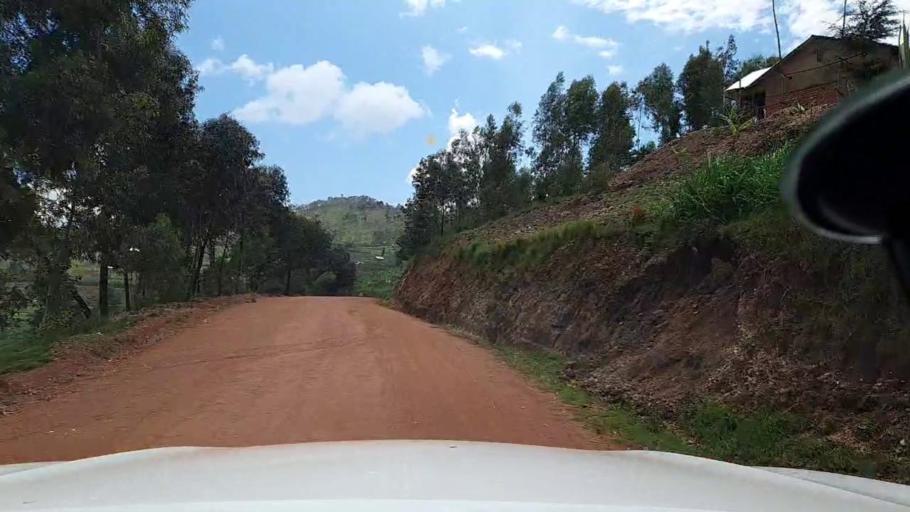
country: RW
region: Kigali
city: Kigali
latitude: -1.7764
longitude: 29.8407
